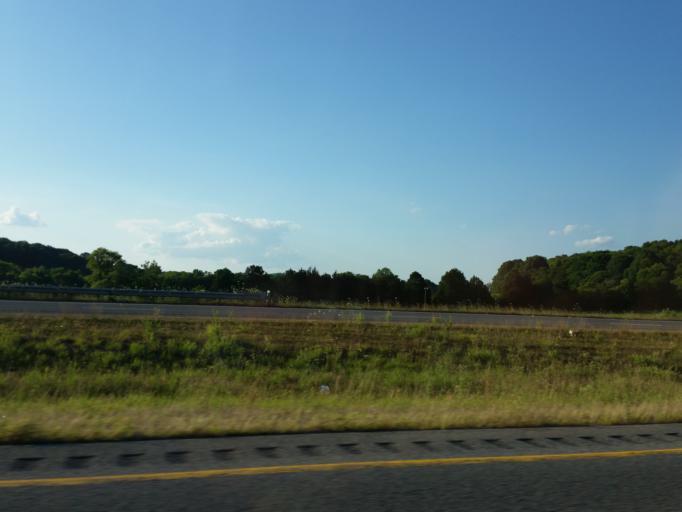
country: US
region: Tennessee
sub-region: Williamson County
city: Nolensville
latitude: 35.8470
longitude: -86.7004
